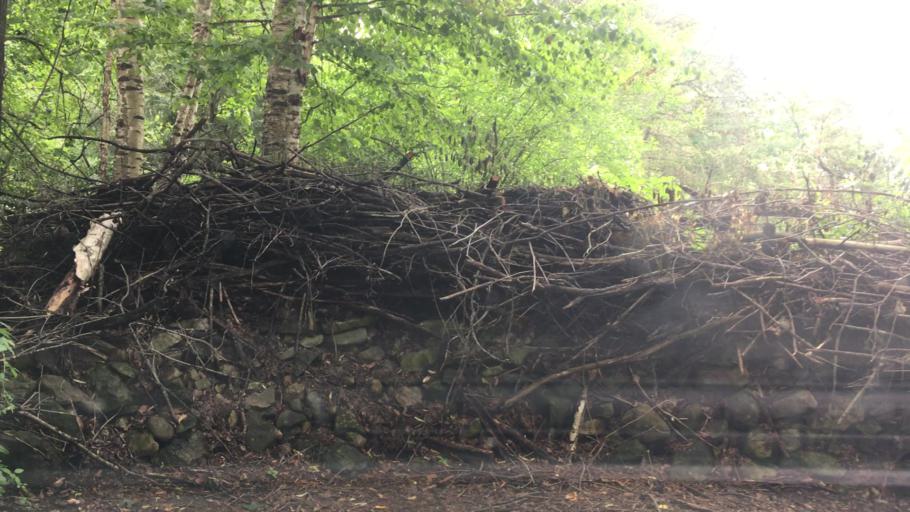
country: US
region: Vermont
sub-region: Bennington County
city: Bennington
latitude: 42.8874
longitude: -73.2196
